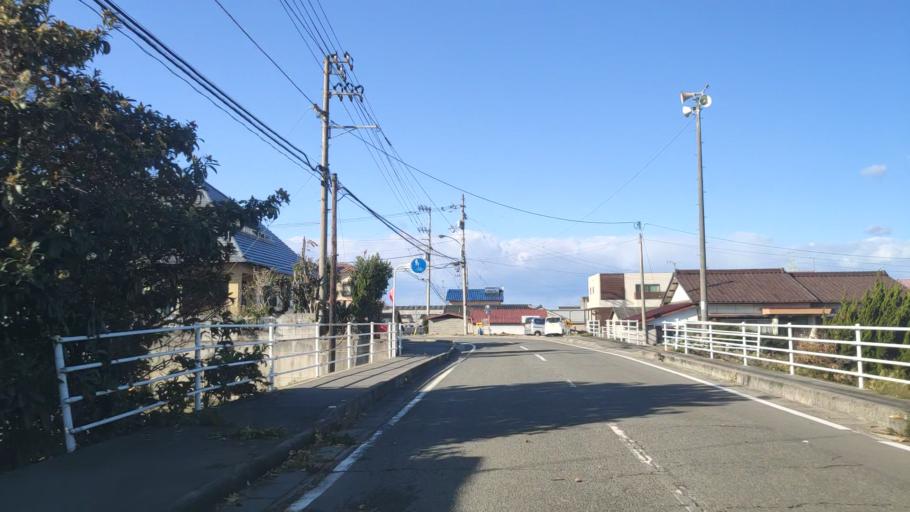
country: JP
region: Ehime
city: Saijo
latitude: 33.9304
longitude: 133.1645
